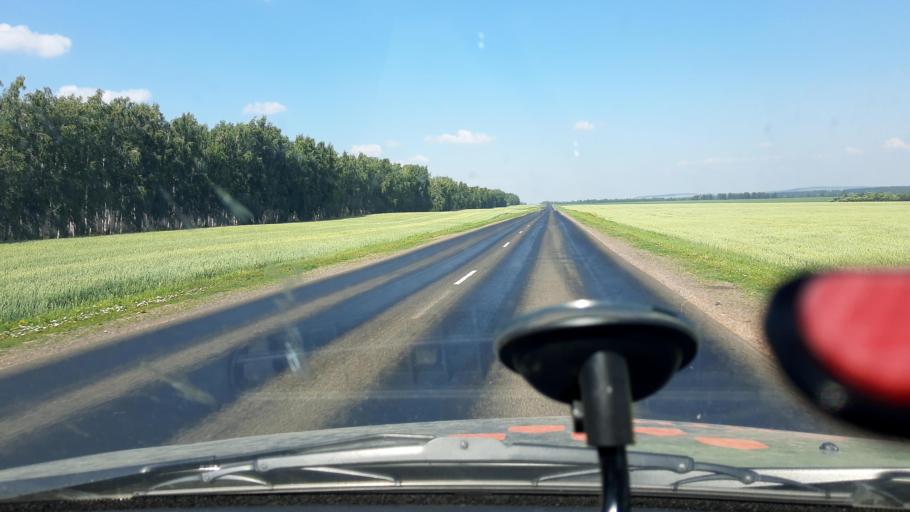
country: RU
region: Bashkortostan
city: Chekmagush
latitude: 55.0790
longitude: 54.6364
